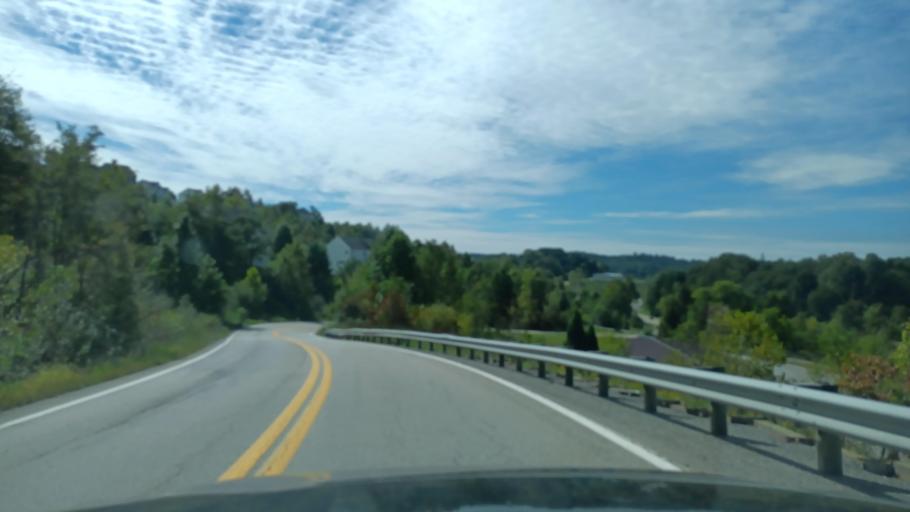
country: US
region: West Virginia
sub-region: Harrison County
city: Bridgeport
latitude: 39.2924
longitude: -80.2232
